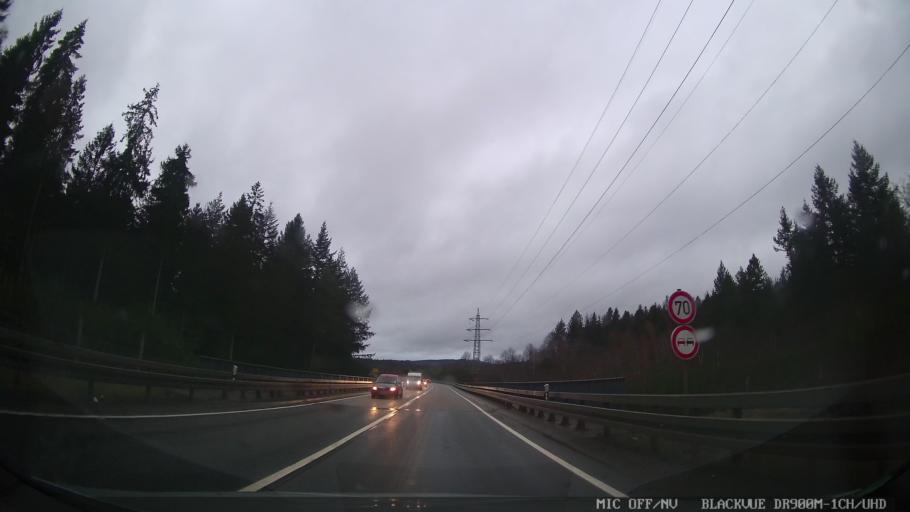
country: DE
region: Saarland
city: Mettlach
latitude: 49.4837
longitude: 6.6150
